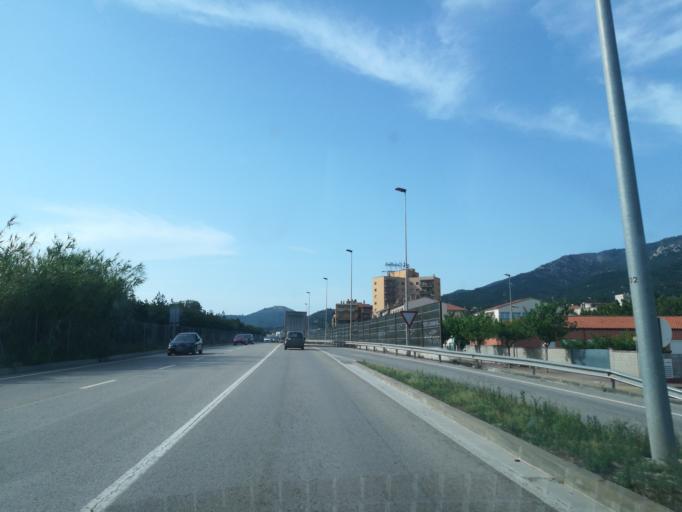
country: ES
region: Catalonia
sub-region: Provincia de Girona
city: la Jonquera
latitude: 42.4179
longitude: 2.8715
